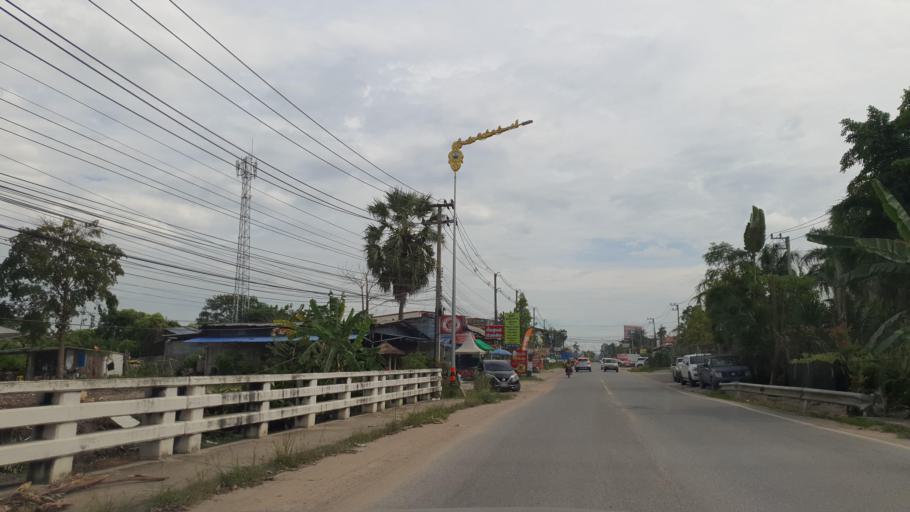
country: TH
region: Chon Buri
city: Phatthaya
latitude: 12.9537
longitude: 100.9288
